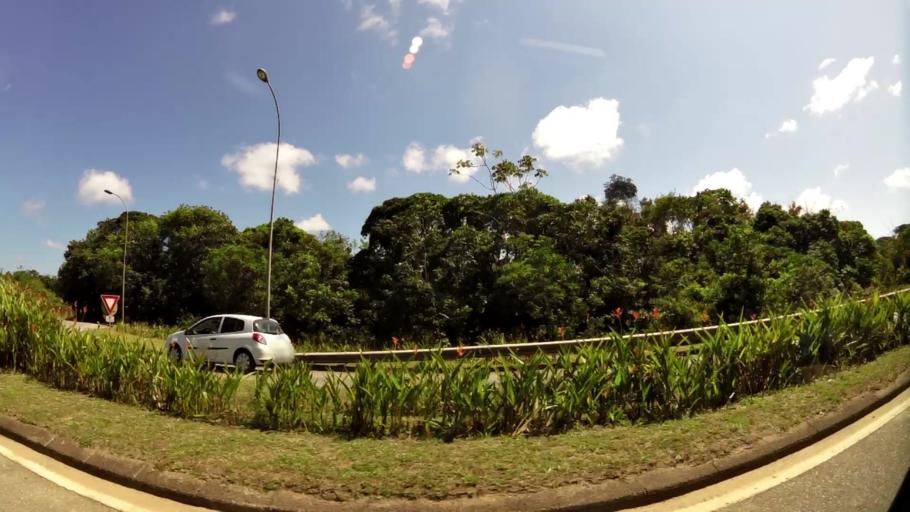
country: GF
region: Guyane
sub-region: Guyane
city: Matoury
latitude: 4.8373
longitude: -52.3384
